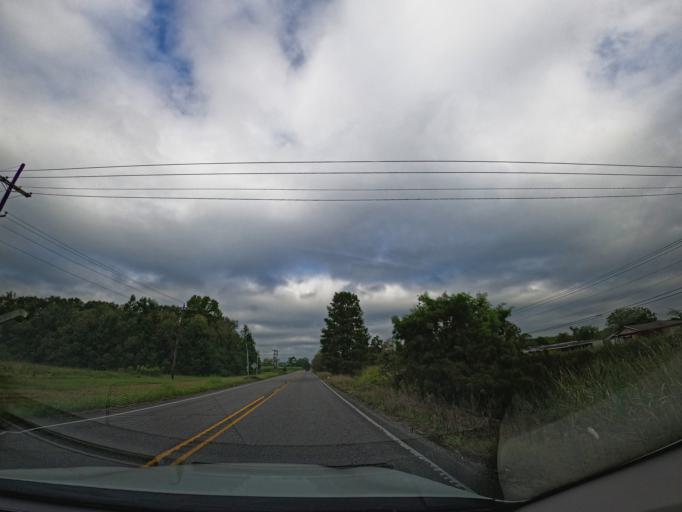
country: US
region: Louisiana
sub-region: Saint Mary Parish
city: Amelia
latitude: 29.6444
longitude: -90.9632
